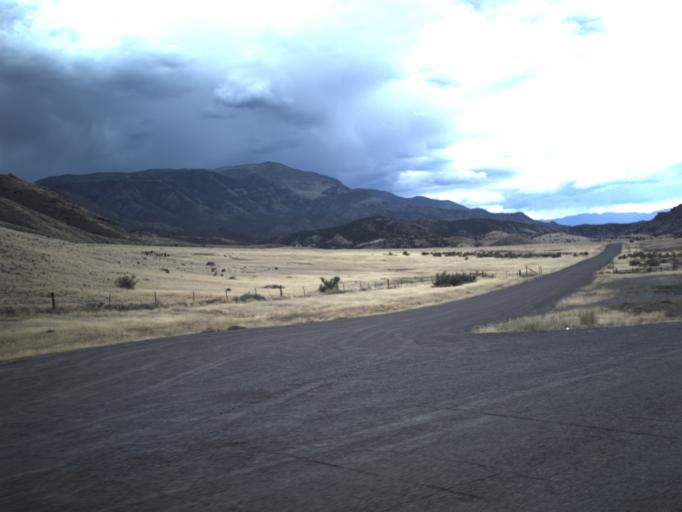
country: US
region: Utah
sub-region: Sevier County
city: Richfield
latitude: 38.7691
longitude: -111.9655
